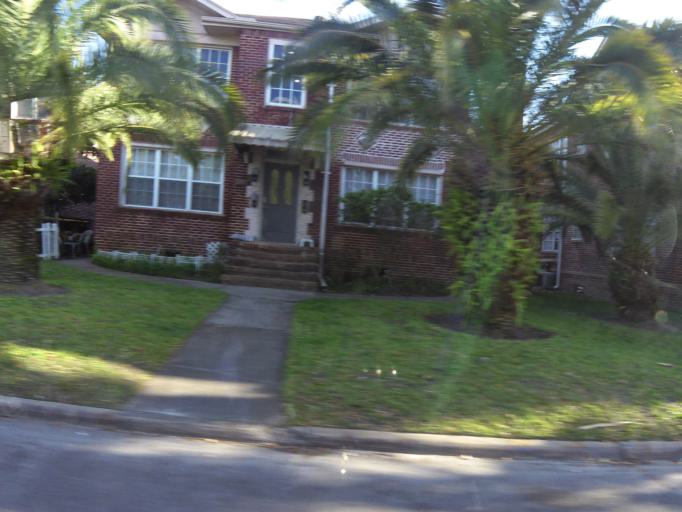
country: US
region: Florida
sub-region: Duval County
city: Jacksonville
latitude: 30.3141
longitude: -81.7018
